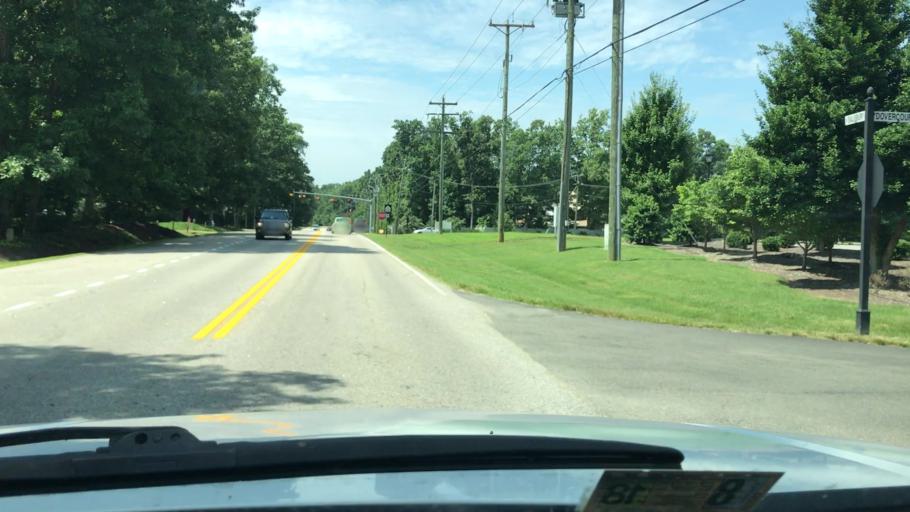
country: US
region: Virginia
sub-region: Chesterfield County
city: Brandermill
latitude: 37.5246
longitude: -77.6638
